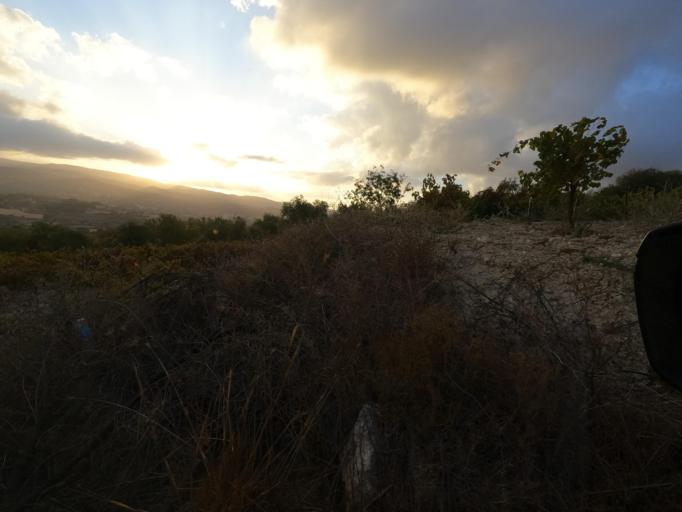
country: CY
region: Pafos
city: Mesogi
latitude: 34.8470
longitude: 32.5342
